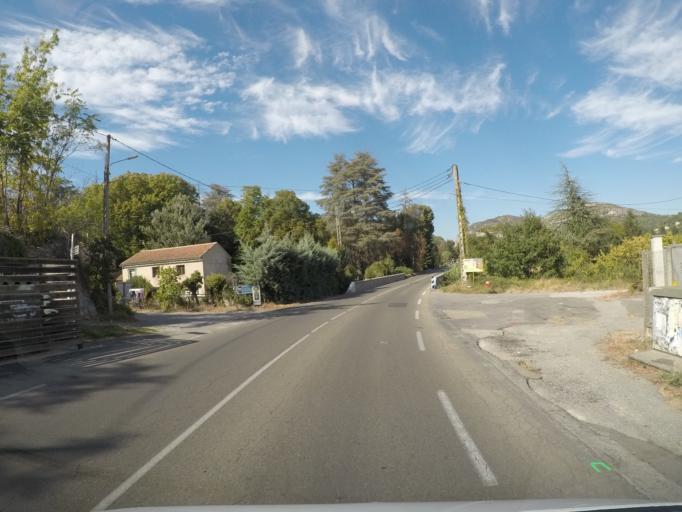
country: FR
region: Languedoc-Roussillon
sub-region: Departement du Gard
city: Anduze
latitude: 44.0416
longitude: 3.9847
